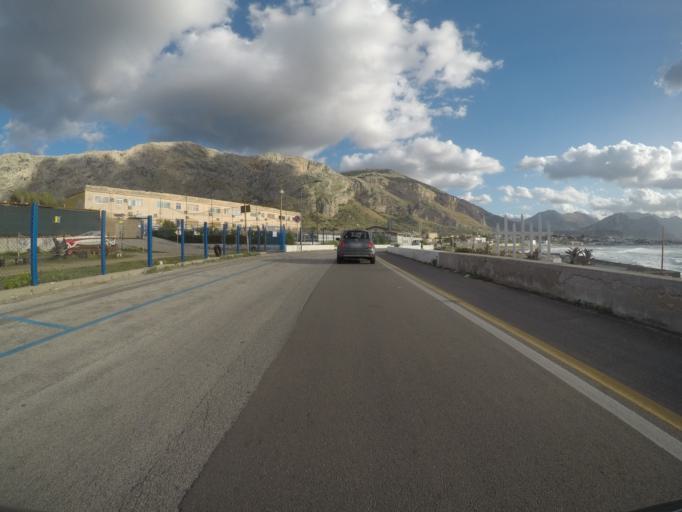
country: IT
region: Sicily
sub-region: Palermo
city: Isola delle Femmine
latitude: 38.1942
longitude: 13.2441
